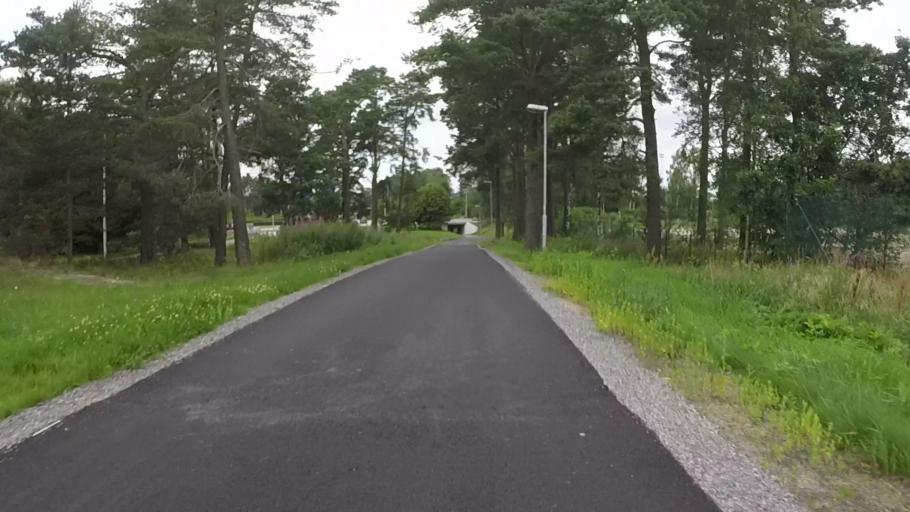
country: SE
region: Vaestra Goetaland
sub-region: Trollhattan
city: Trollhattan
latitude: 58.2794
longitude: 12.3081
